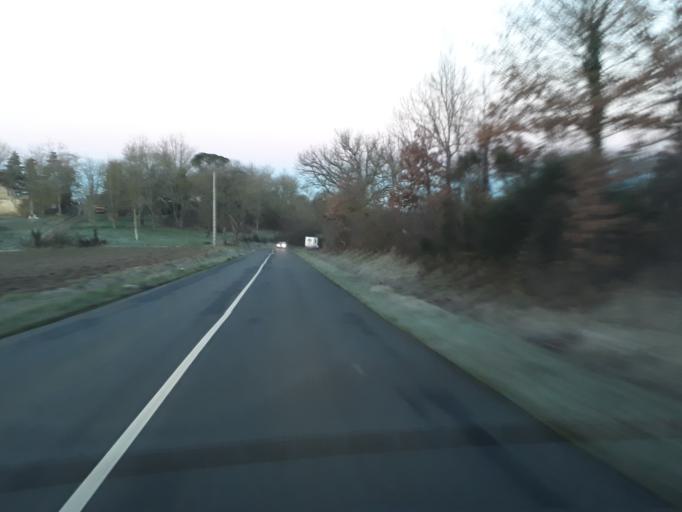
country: FR
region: Midi-Pyrenees
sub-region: Departement du Gers
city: Lombez
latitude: 43.5271
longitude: 0.8587
